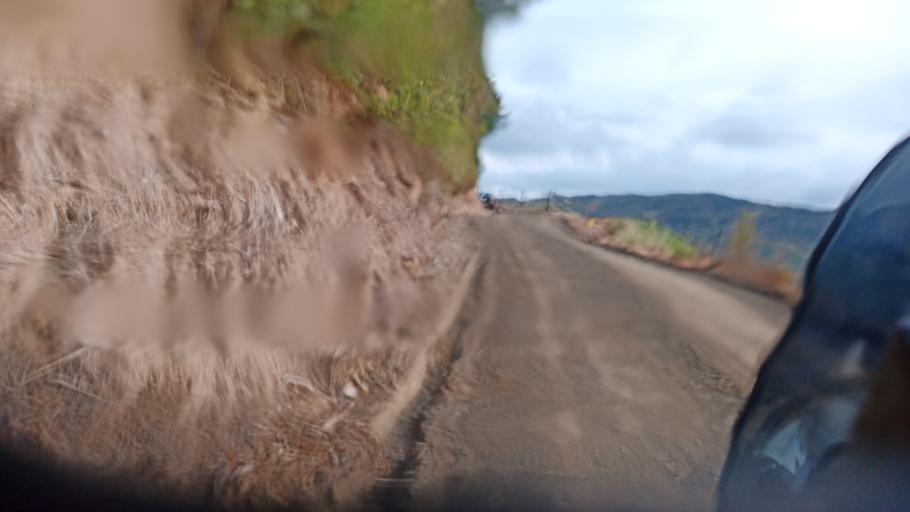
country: NZ
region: Gisborne
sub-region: Gisborne District
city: Gisborne
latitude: -38.4593
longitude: 177.5389
